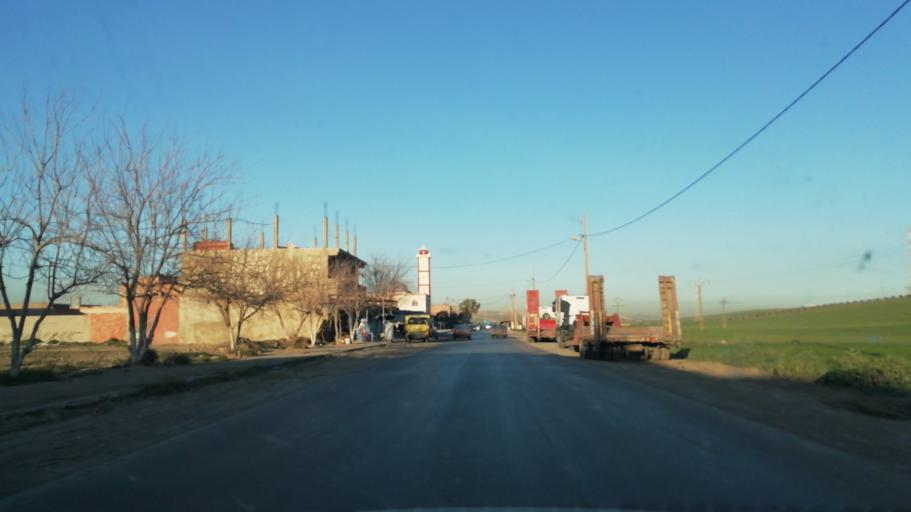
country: DZ
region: Oran
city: Es Senia
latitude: 35.5602
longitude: -0.5668
